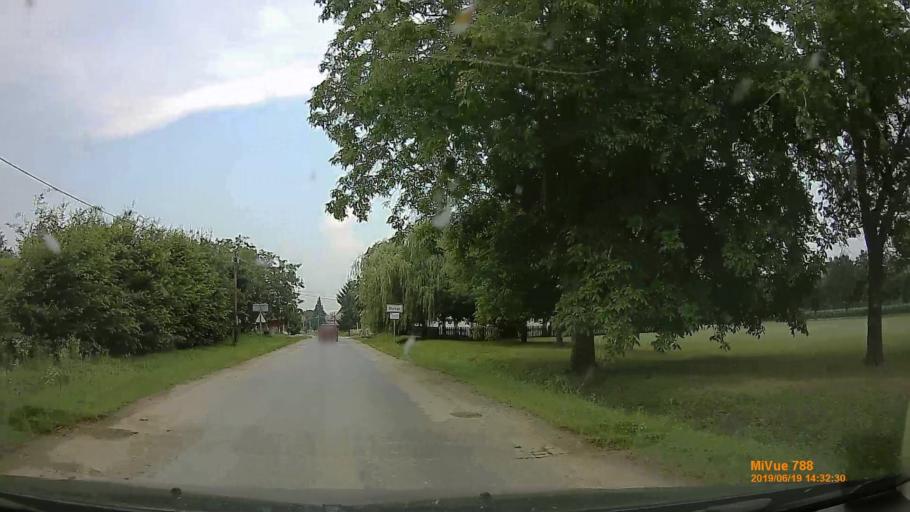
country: HU
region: Baranya
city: Szigetvar
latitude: 46.0731
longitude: 17.7783
